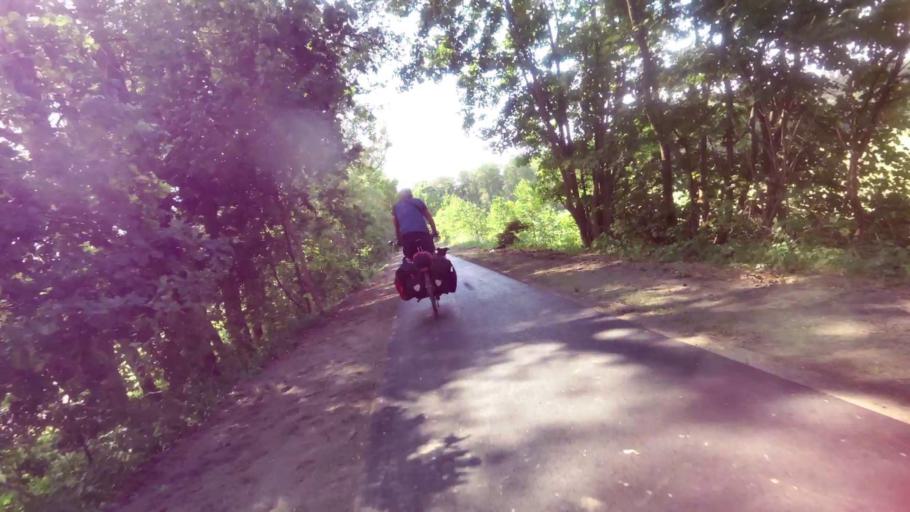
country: PL
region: West Pomeranian Voivodeship
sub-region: Powiat gryfinski
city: Gryfino
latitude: 53.2241
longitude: 14.5493
